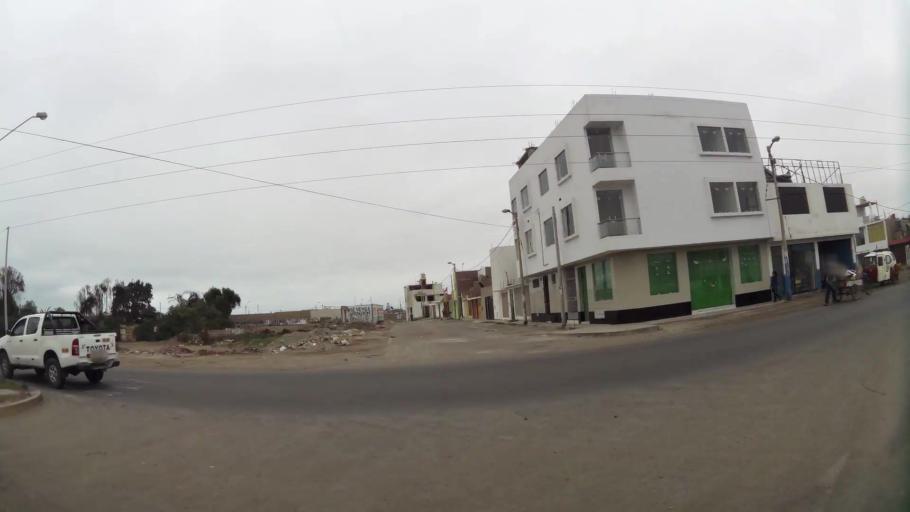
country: PE
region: Ica
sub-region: Provincia de Pisco
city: Pisco
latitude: -13.7169
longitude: -76.2104
